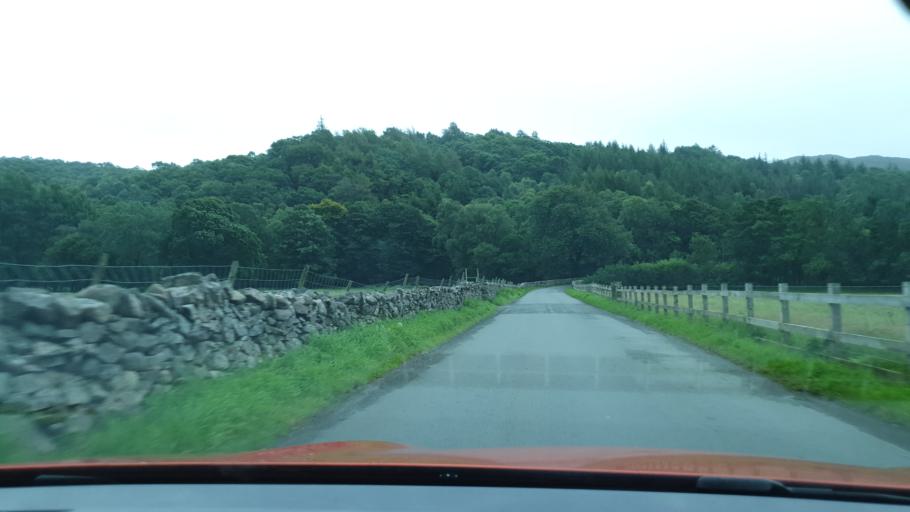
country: GB
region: England
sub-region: Cumbria
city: Seascale
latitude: 54.3853
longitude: -3.3122
